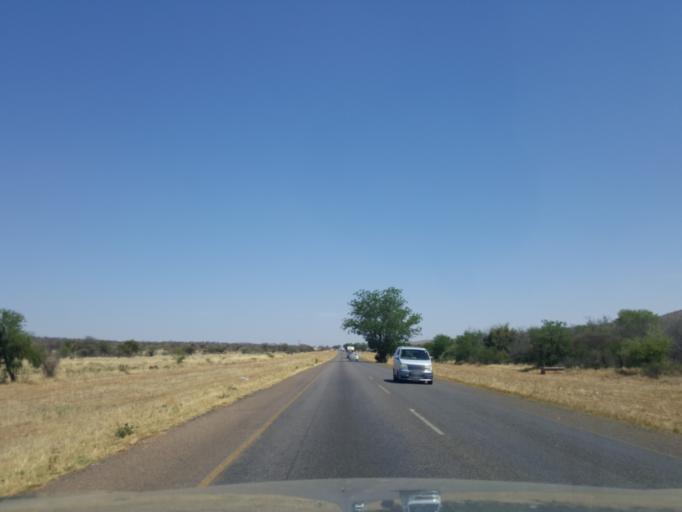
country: BW
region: South East
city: Lobatse
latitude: -25.1617
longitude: 25.6887
